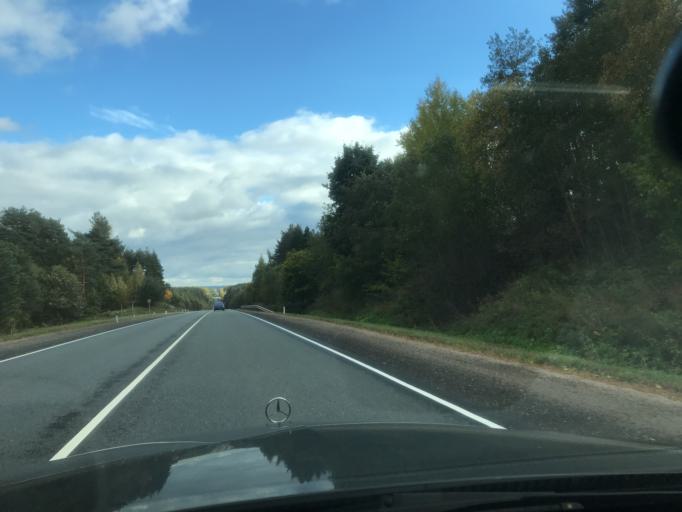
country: RU
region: Pskov
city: Opochka
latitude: 56.6417
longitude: 28.7839
